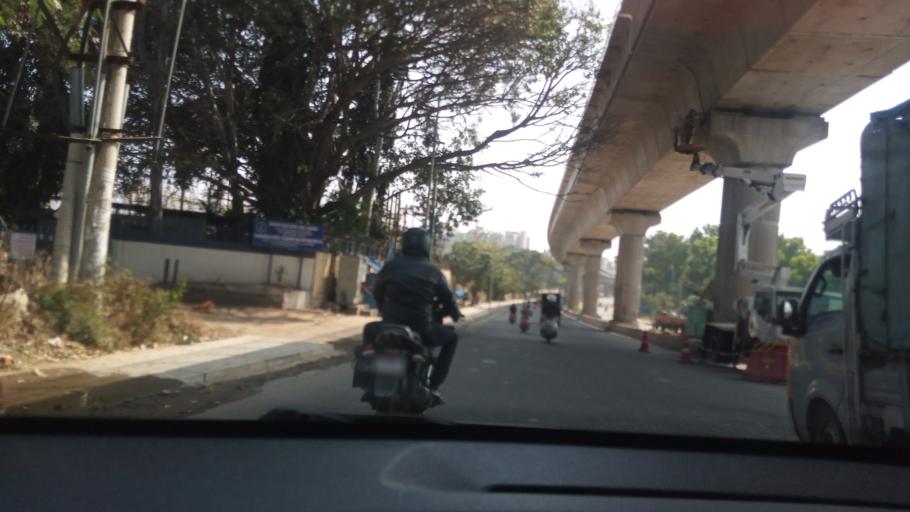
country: IN
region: Karnataka
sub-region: Bangalore Urban
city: Bangalore
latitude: 12.9930
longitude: 77.7090
